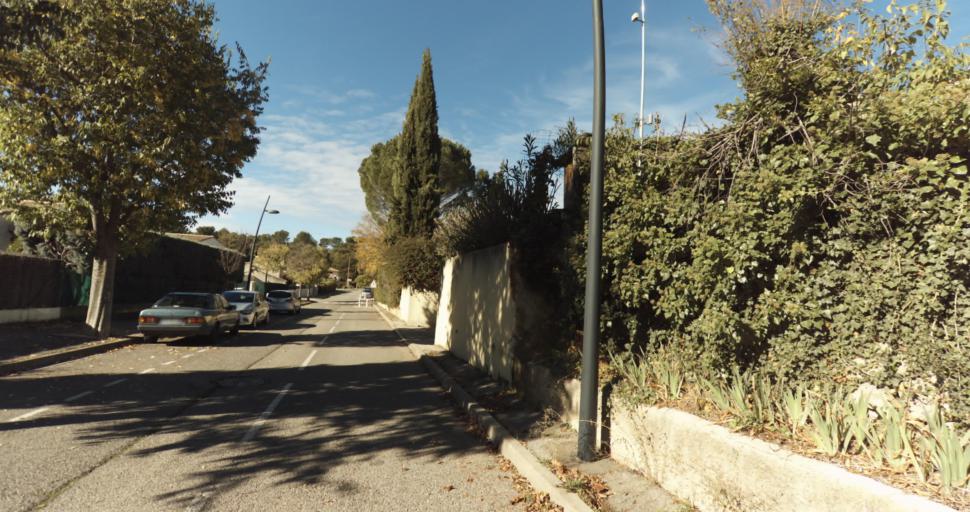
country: FR
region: Provence-Alpes-Cote d'Azur
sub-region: Departement des Bouches-du-Rhone
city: Venelles
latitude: 43.5960
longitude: 5.4776
